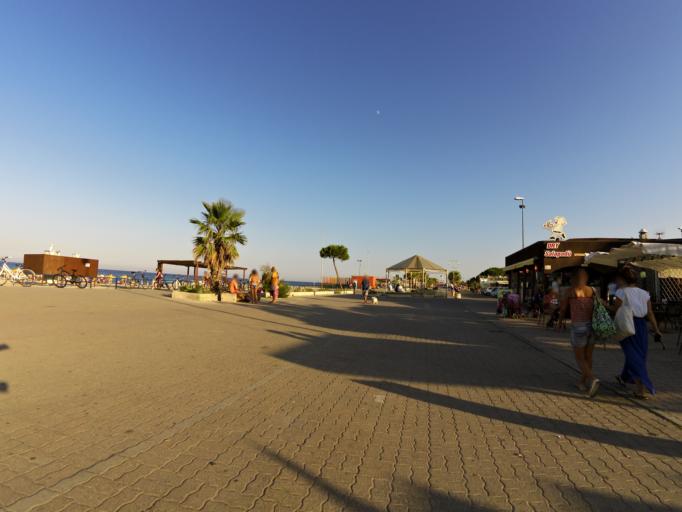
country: IT
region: Calabria
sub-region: Provincia di Catanzaro
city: Soverato Marina
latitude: 38.6885
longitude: 16.5552
